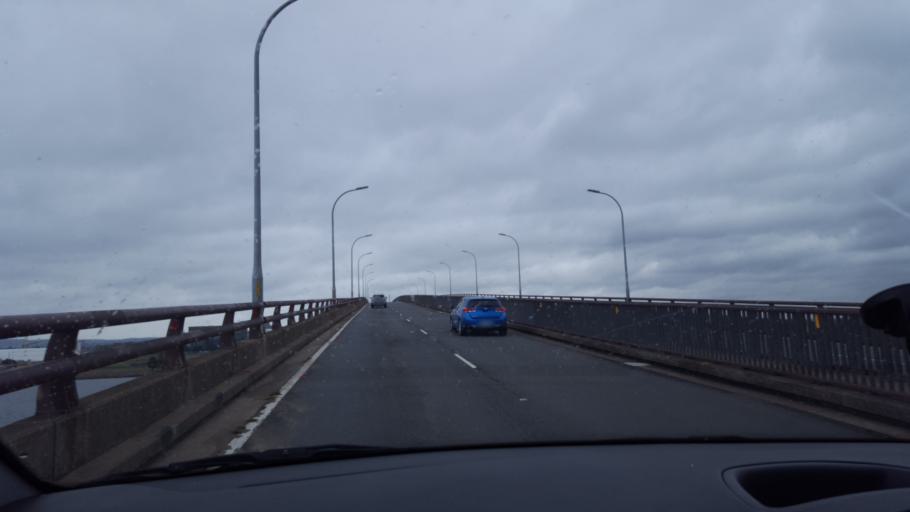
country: AU
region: New South Wales
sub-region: Newcastle
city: Carrington
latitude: -32.8847
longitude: 151.7900
